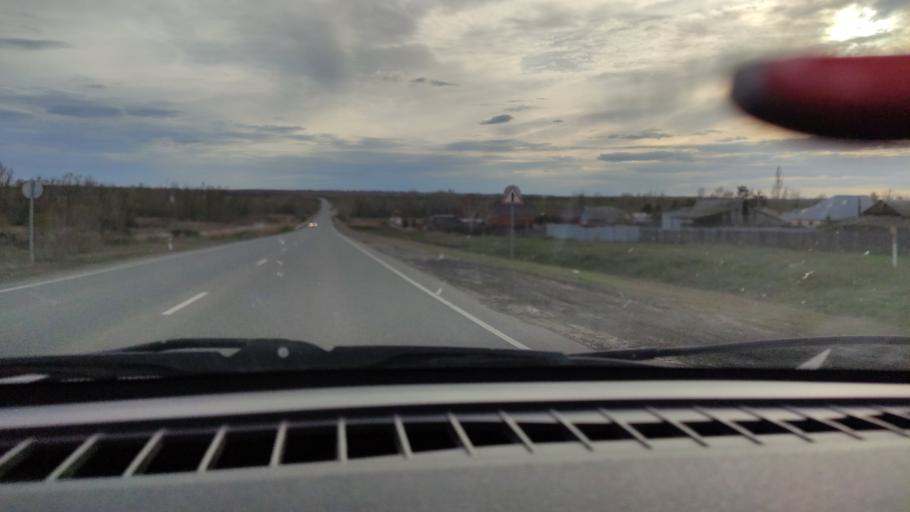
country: RU
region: Orenburg
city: Tatarskaya Kargala
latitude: 52.0251
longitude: 55.2250
